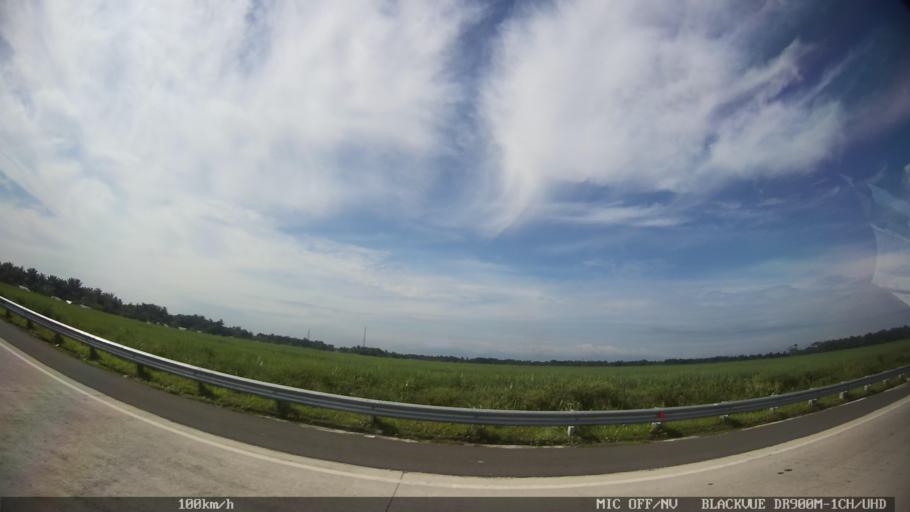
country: ID
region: North Sumatra
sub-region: Kabupaten Langkat
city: Stabat
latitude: 3.7133
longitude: 98.5237
